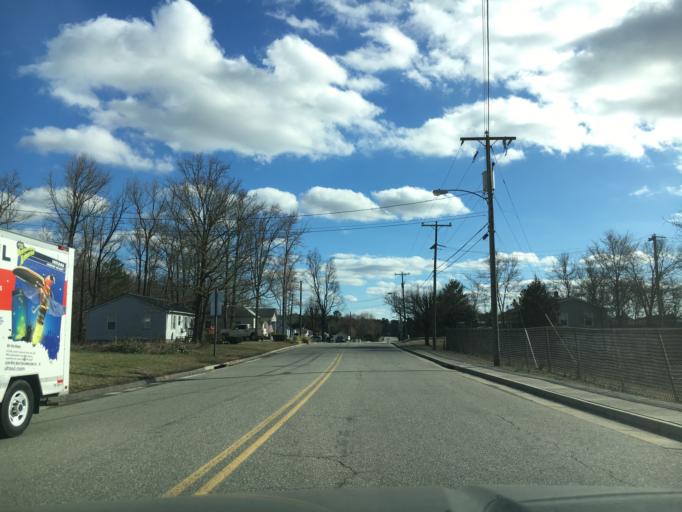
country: US
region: Virginia
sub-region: Halifax County
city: South Boston
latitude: 36.7182
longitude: -78.8889
